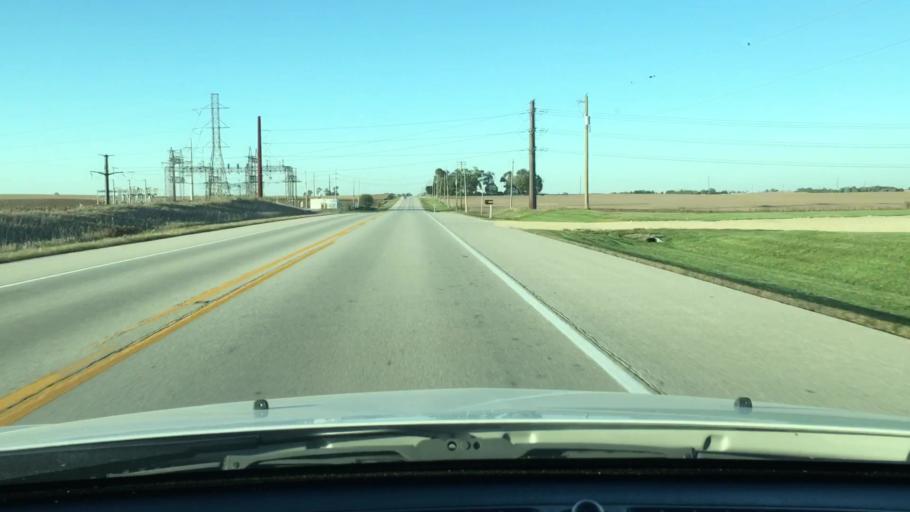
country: US
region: Illinois
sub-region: DeKalb County
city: Waterman
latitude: 41.8251
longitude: -88.7539
